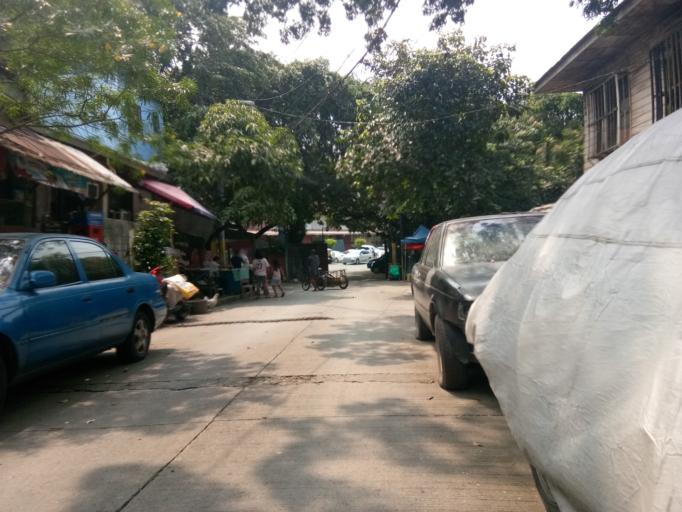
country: PH
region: Metro Manila
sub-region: San Juan
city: San Juan
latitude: 14.6133
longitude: 121.0506
